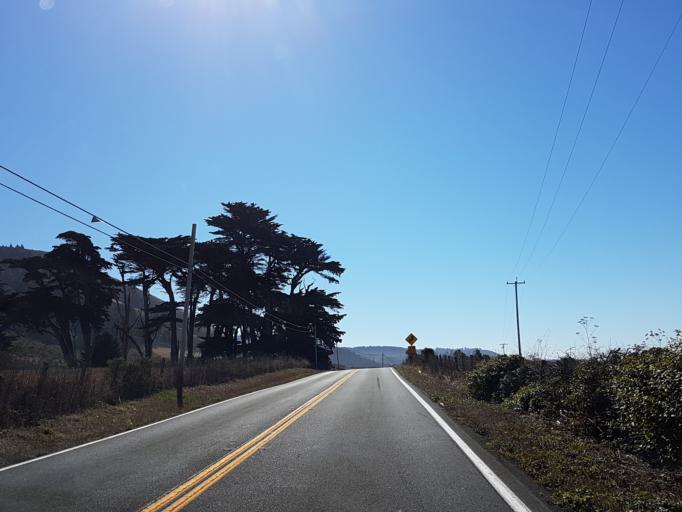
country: US
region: California
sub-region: Mendocino County
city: Boonville
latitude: 39.0780
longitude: -123.6952
